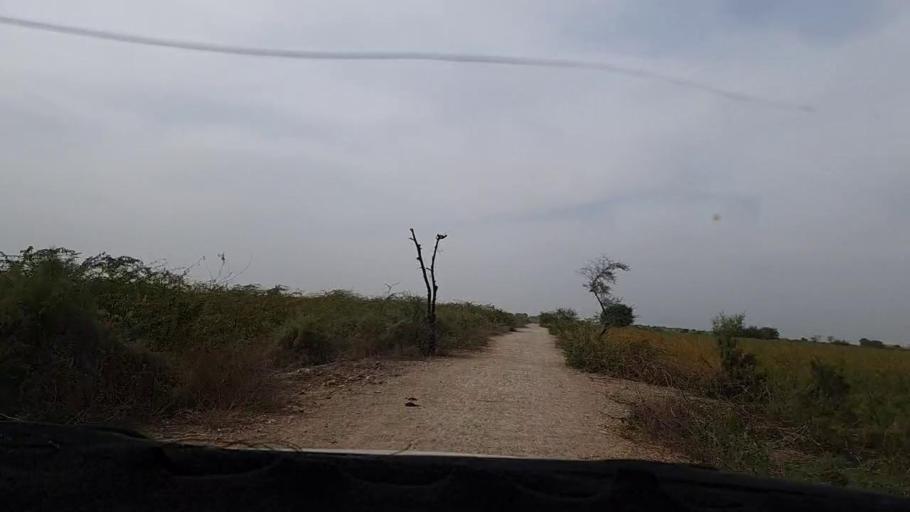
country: PK
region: Sindh
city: Pithoro
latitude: 25.5564
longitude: 69.3424
